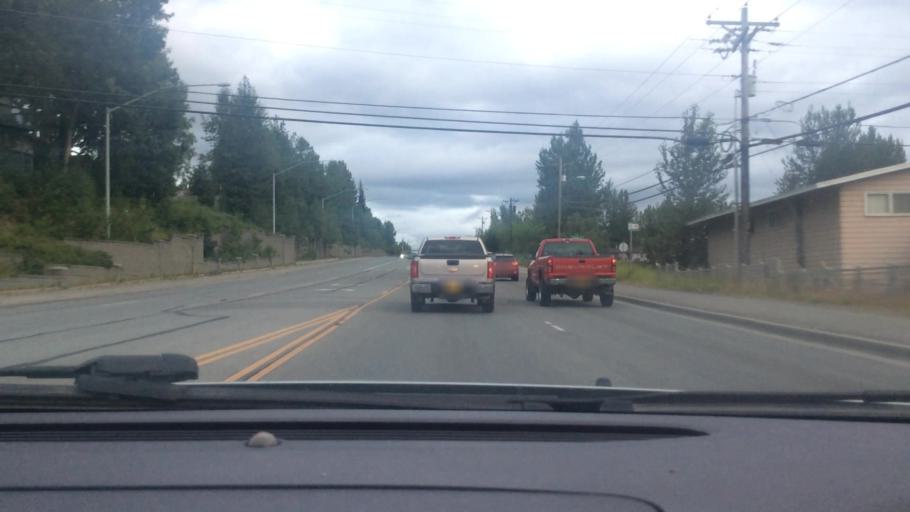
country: US
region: Alaska
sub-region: Anchorage Municipality
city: Elmendorf Air Force Base
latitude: 61.2064
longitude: -149.7335
